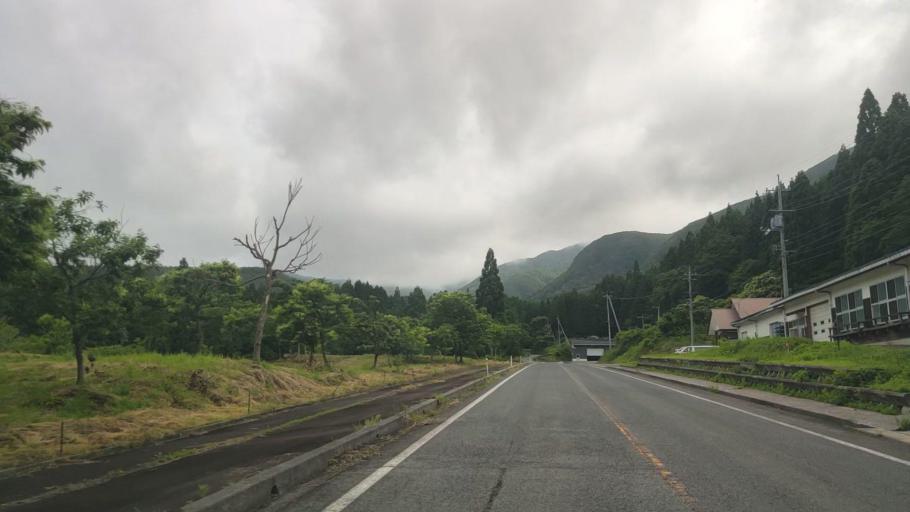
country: JP
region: Tottori
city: Yonago
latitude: 35.3259
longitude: 133.5567
